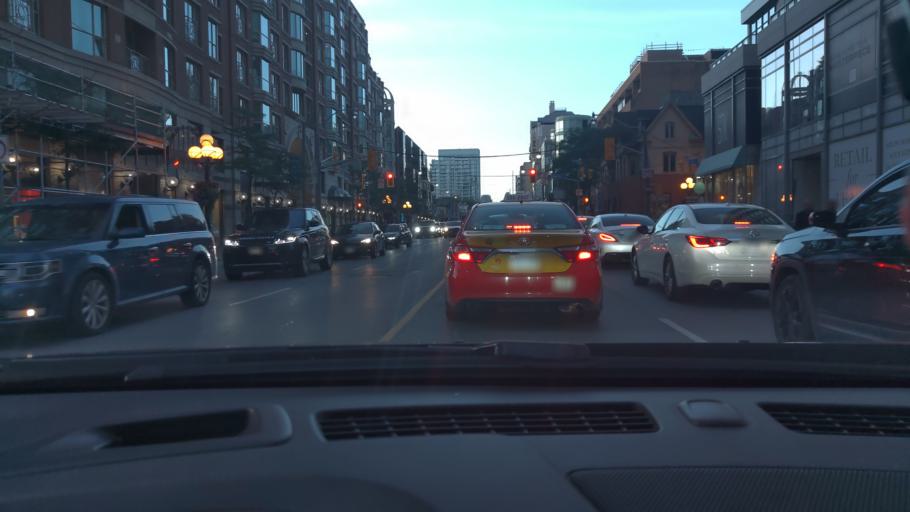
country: CA
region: Ontario
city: Toronto
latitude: 43.6700
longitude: -79.3947
